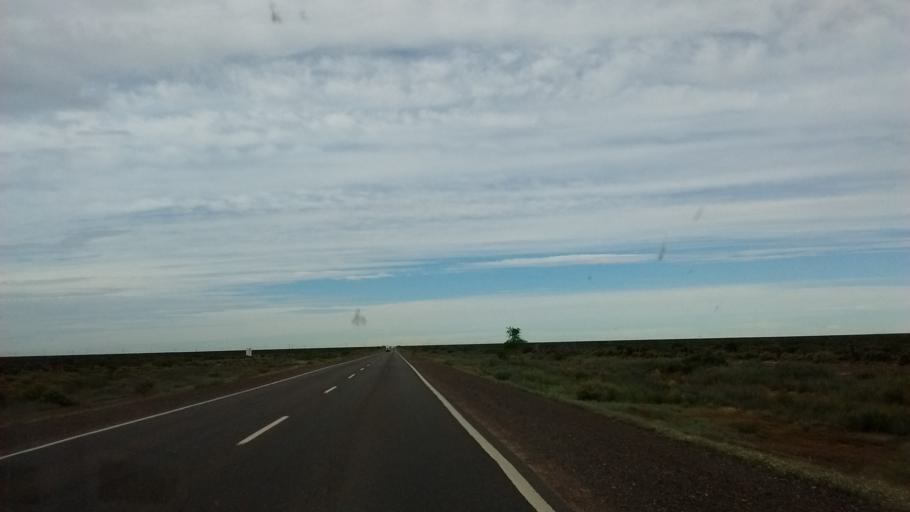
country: AR
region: Rio Negro
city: Contraalmirante Cordero
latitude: -38.5048
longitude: -68.0657
